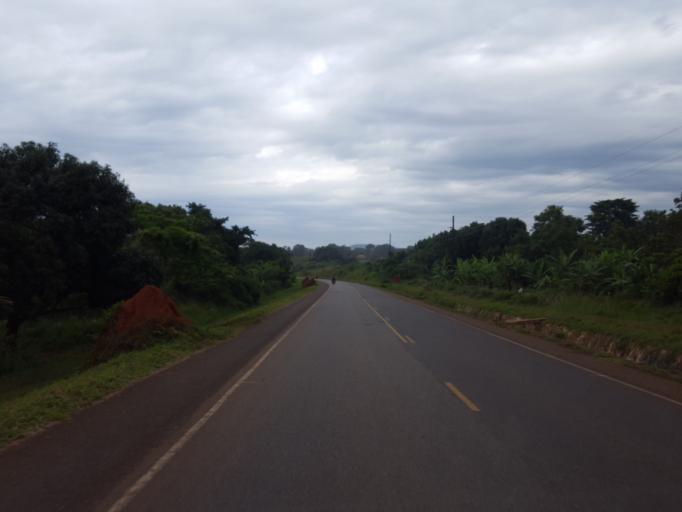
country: UG
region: Central Region
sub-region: Kiboga District
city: Kiboga
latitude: 0.9626
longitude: 31.7411
